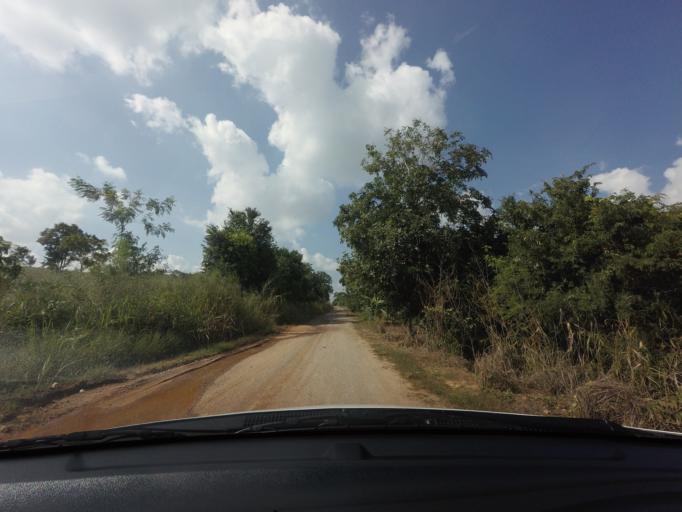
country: TH
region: Nakhon Ratchasima
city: Wang Nam Khiao
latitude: 14.5010
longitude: 101.6300
